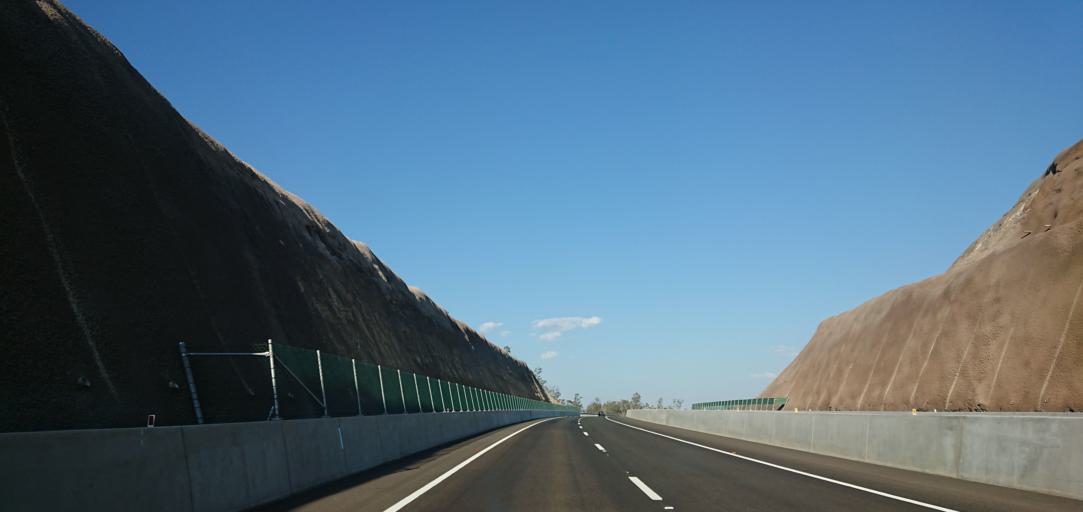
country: AU
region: Queensland
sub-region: Toowoomba
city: East Toowoomba
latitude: -27.5146
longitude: 152.0406
